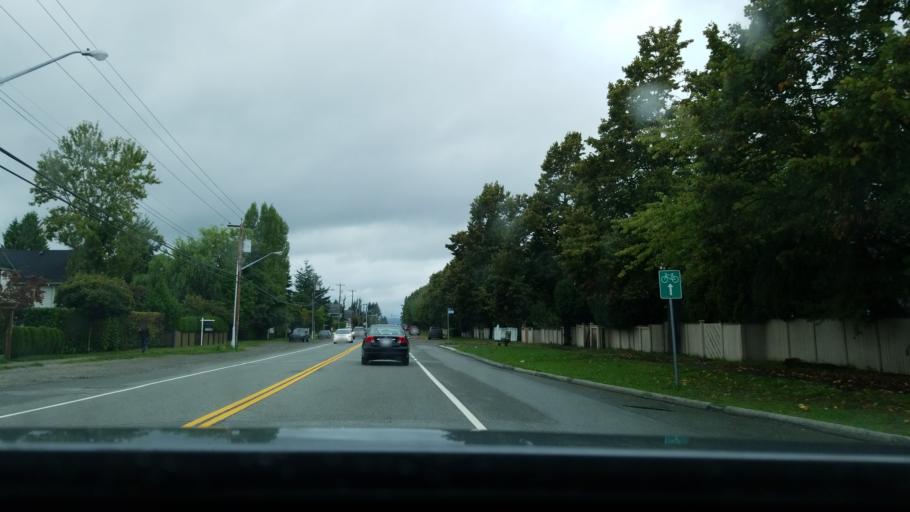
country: CA
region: British Columbia
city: Langley
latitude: 49.1189
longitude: -122.7073
